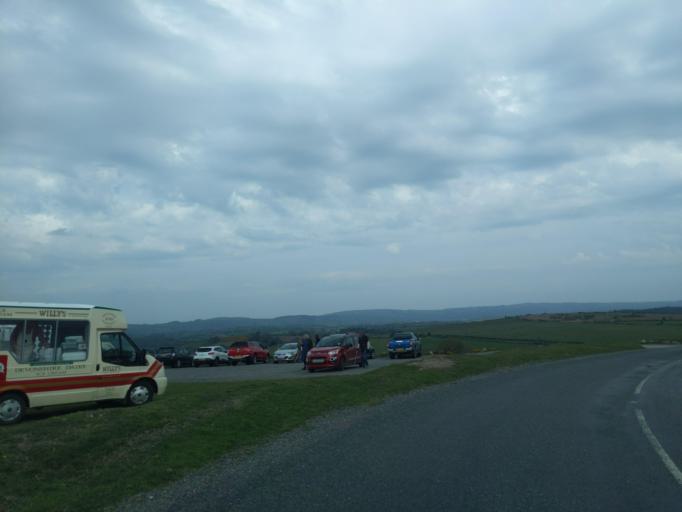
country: GB
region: England
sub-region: Devon
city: Ashburton
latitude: 50.6360
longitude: -3.8426
